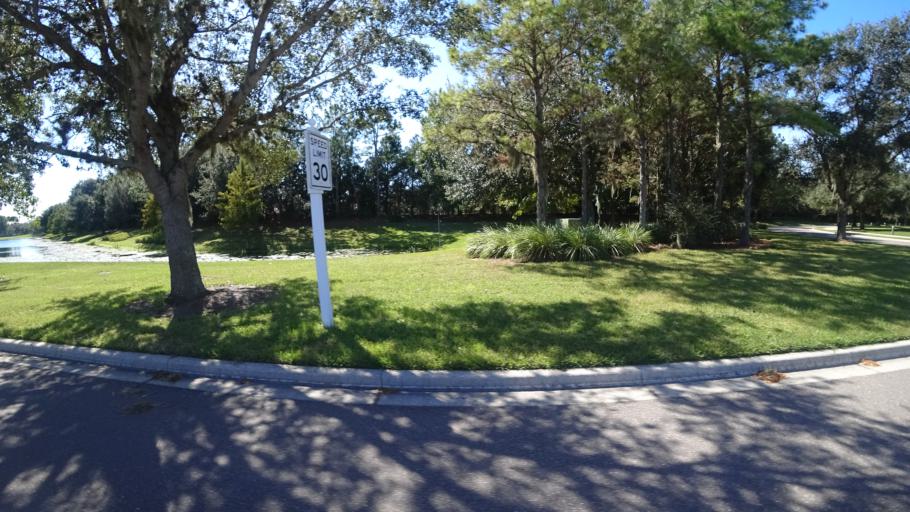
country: US
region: Florida
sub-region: Sarasota County
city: The Meadows
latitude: 27.4015
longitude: -82.4114
